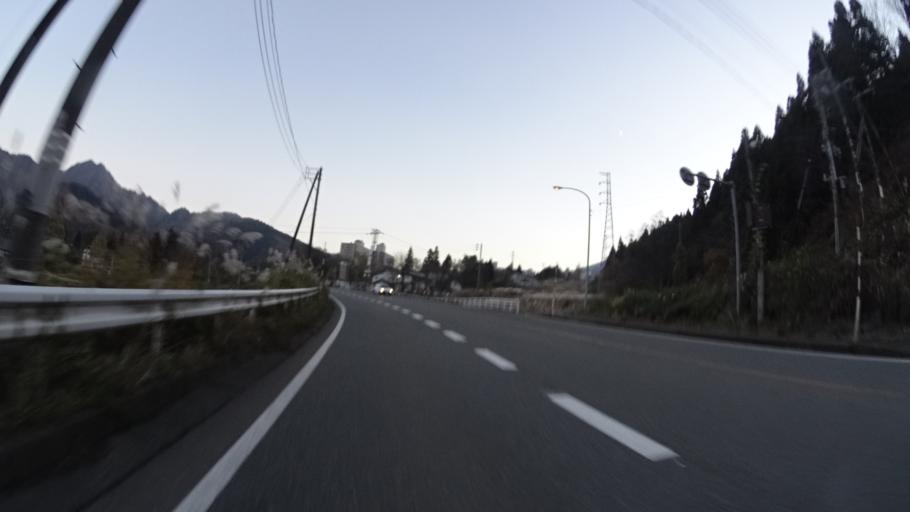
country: JP
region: Niigata
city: Shiozawa
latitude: 36.9730
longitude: 138.8003
